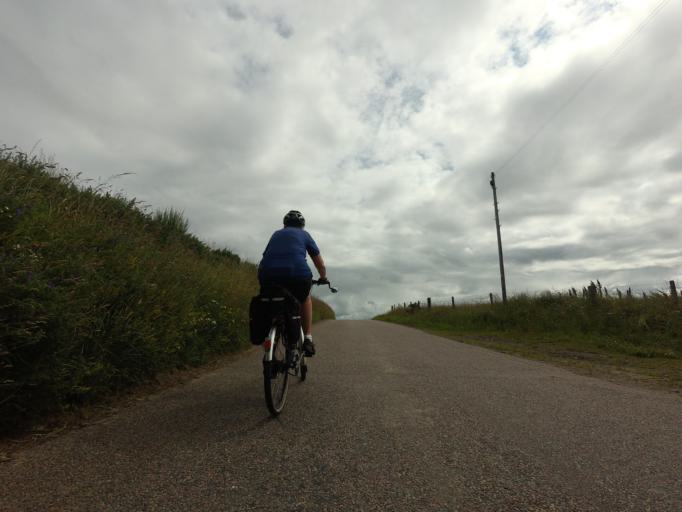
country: GB
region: Scotland
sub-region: Moray
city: Fochabers
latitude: 57.6669
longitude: -3.1479
